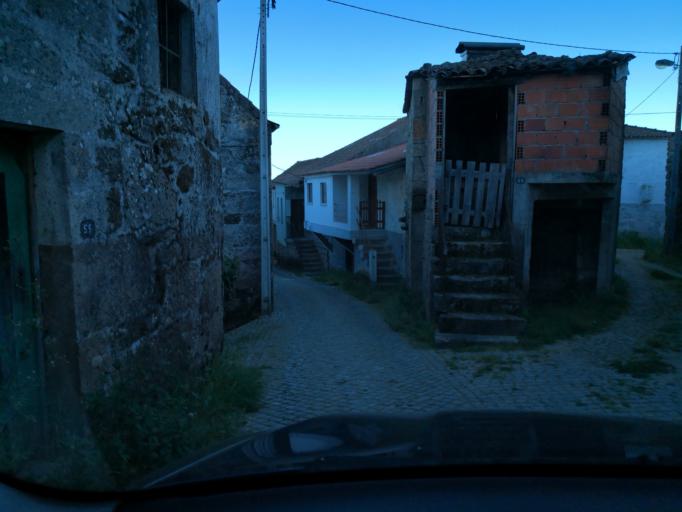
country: PT
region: Vila Real
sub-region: Vila Real
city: Vila Real
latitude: 41.3486
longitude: -7.7298
